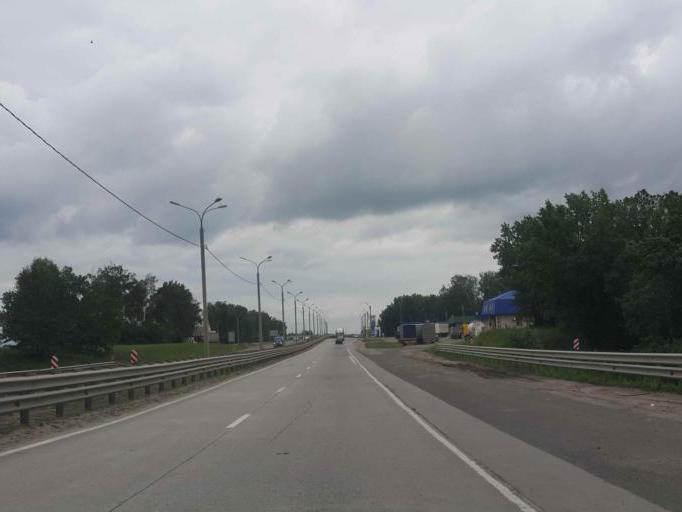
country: RU
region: Tambov
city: Komsomolets
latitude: 52.7346
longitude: 41.2839
